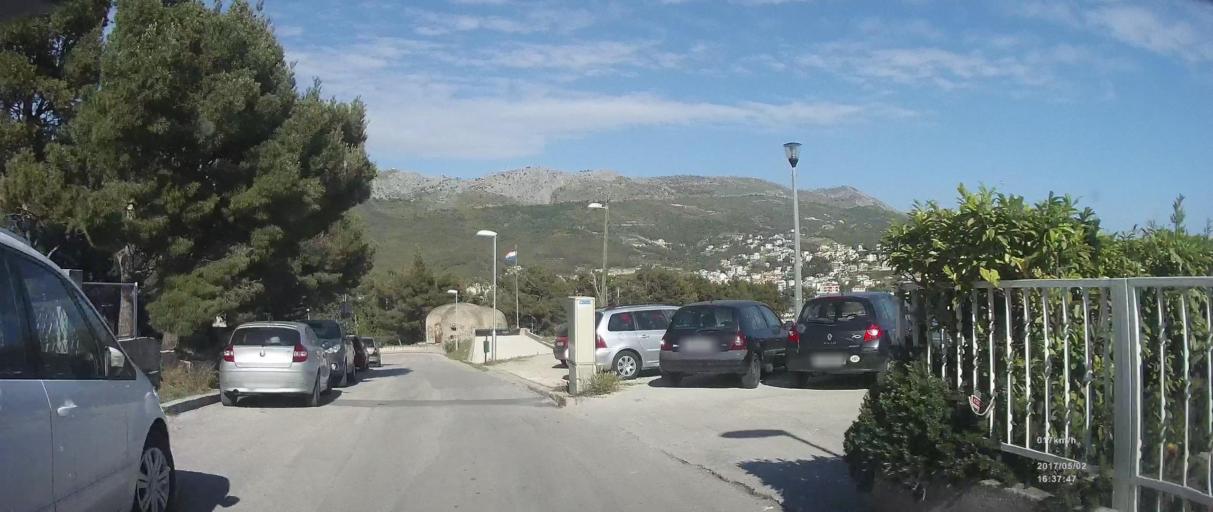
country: HR
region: Splitsko-Dalmatinska
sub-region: Grad Split
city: Stobrec
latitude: 43.5030
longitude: 16.5249
